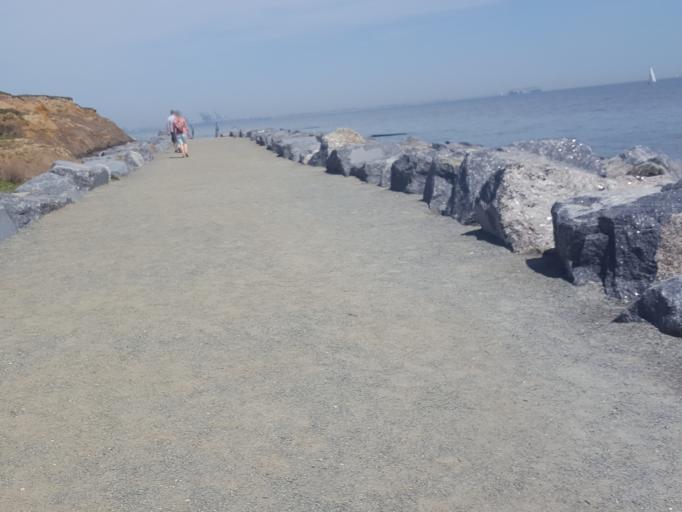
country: GB
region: England
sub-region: Essex
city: Walton-on-the-Naze
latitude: 51.8640
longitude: 1.2897
